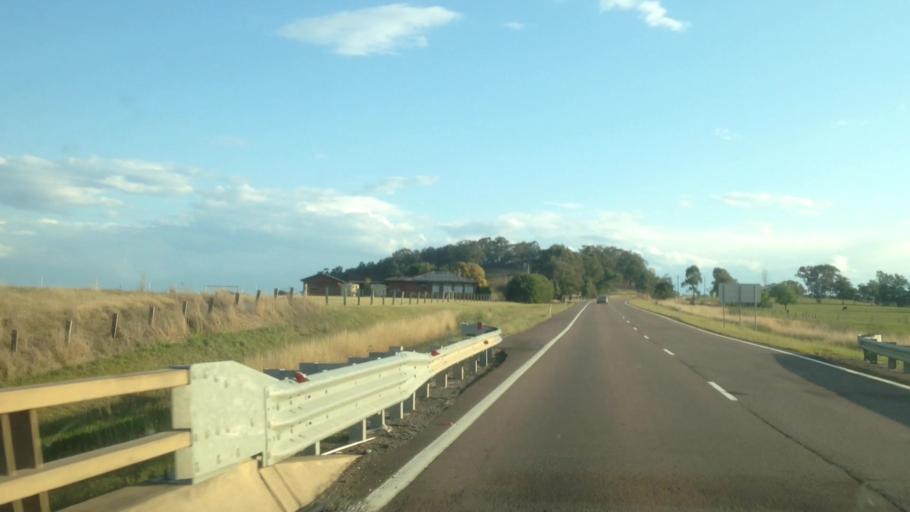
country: AU
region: New South Wales
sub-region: Cessnock
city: Kurri Kurri
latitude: -32.8787
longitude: 151.4741
